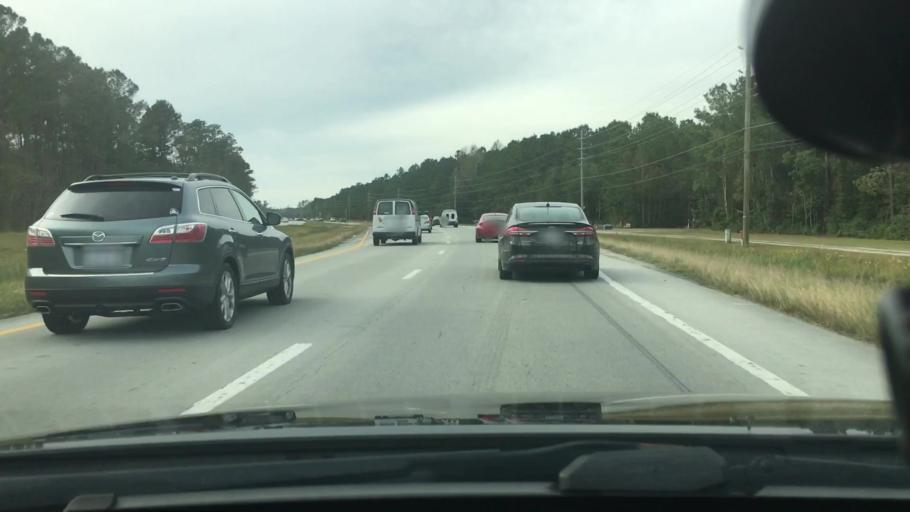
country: US
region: North Carolina
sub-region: Craven County
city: Neuse Forest
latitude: 34.9620
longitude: -76.9549
